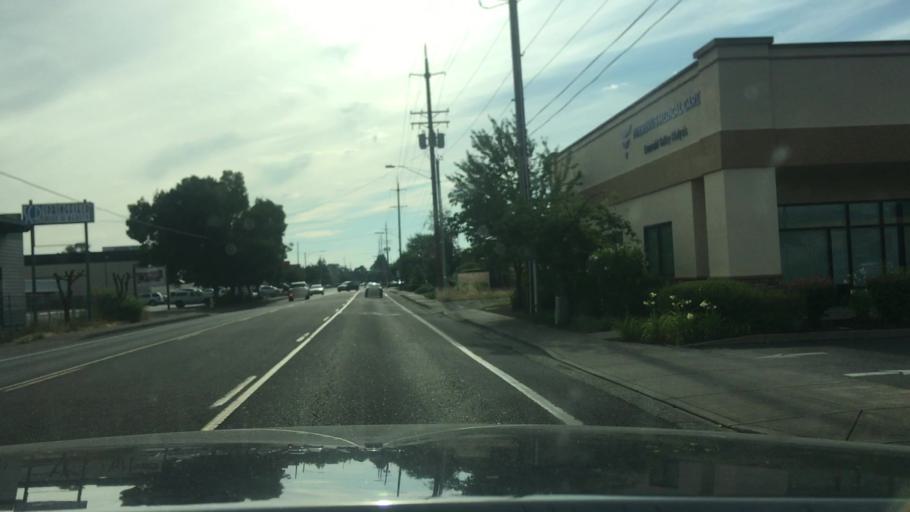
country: US
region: Oregon
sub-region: Lane County
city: Springfield
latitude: 44.0621
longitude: -123.0211
